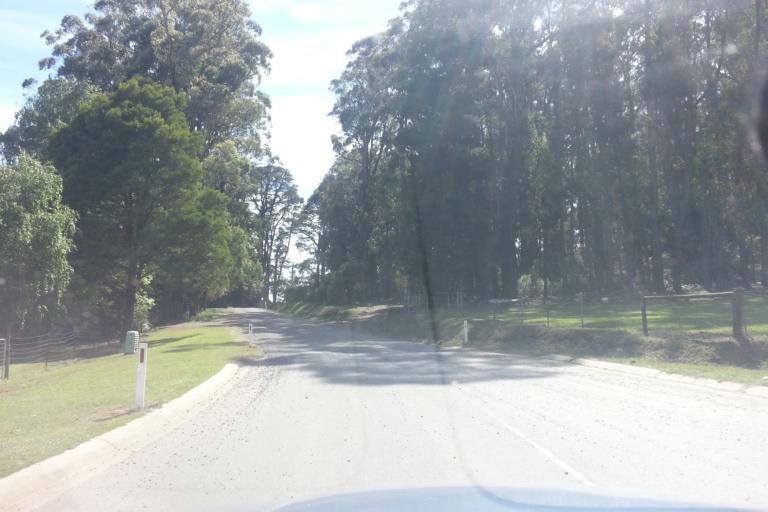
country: AU
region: Victoria
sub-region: Cardinia
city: Gembrook
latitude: -37.9554
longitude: 145.5676
